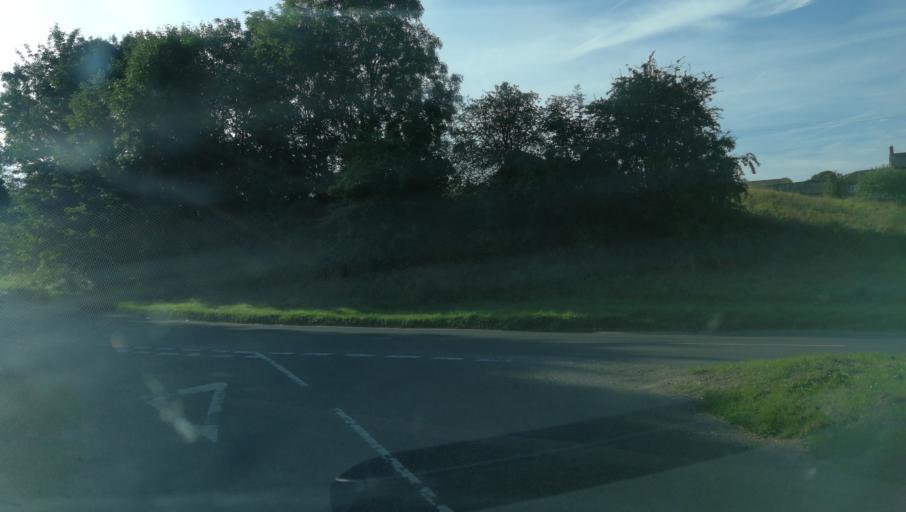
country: GB
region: England
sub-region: Oxfordshire
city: Bloxham
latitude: 52.0318
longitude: -1.4127
